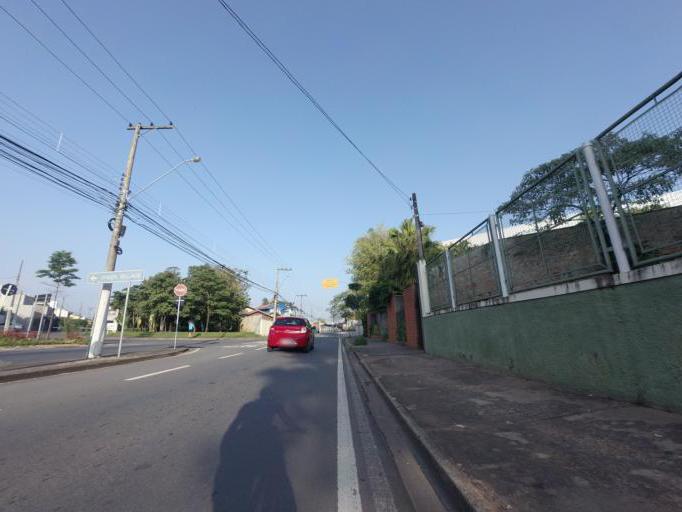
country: BR
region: Sao Paulo
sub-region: Piracicaba
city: Piracicaba
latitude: -22.7411
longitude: -47.6079
